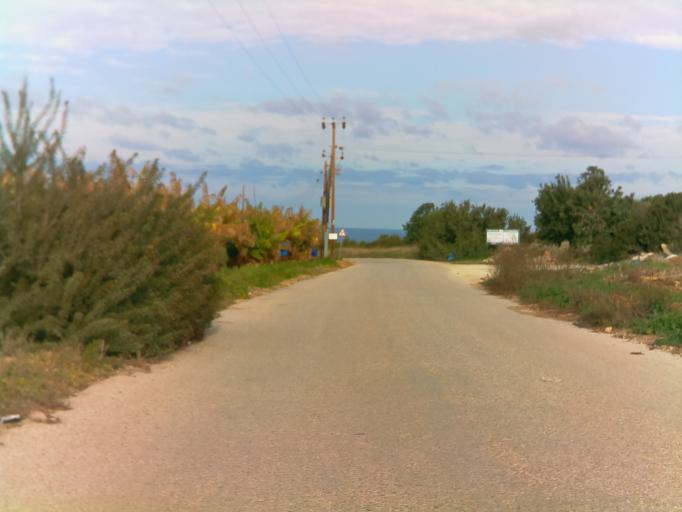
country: CY
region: Pafos
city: Pegeia
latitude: 34.9037
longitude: 32.3271
